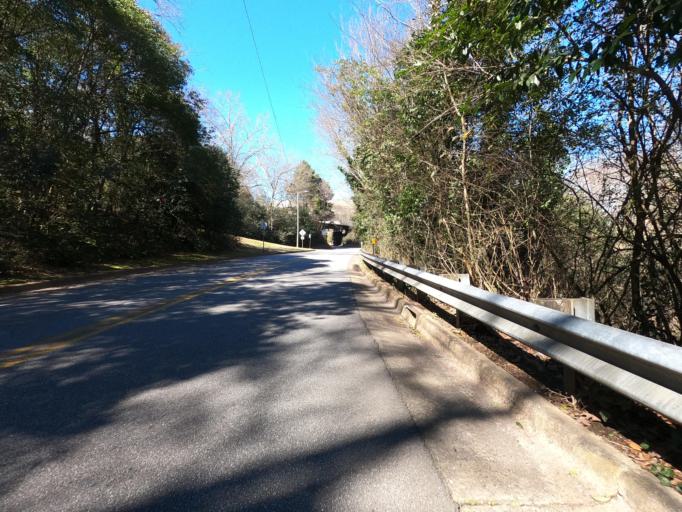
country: US
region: Georgia
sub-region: Clarke County
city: Athens
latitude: 33.9478
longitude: -83.3709
